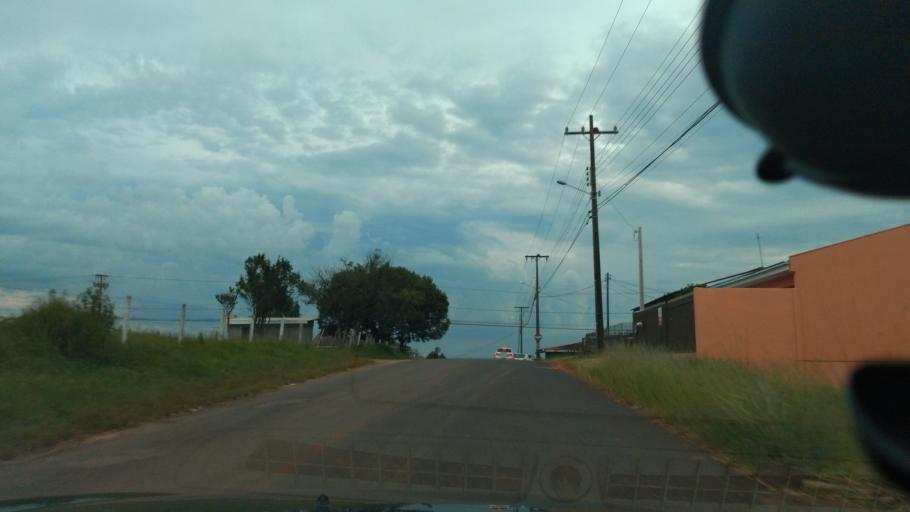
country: BR
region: Parana
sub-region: Guarapuava
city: Guarapuava
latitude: -25.3918
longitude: -51.4856
